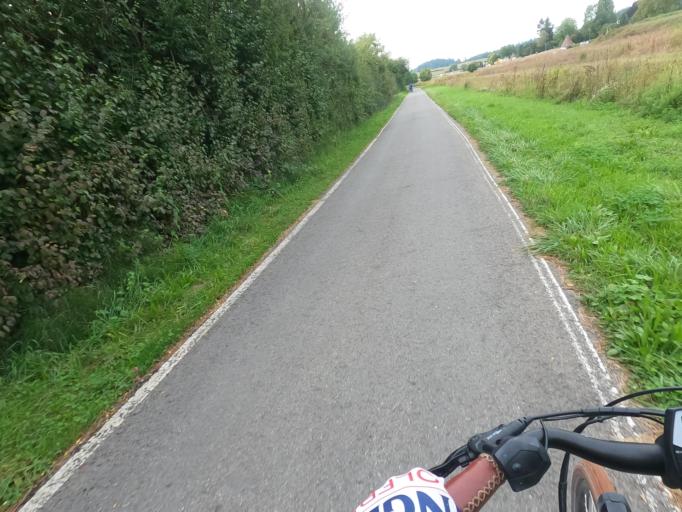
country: DE
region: Baden-Wuerttemberg
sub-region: Freiburg Region
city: Allensbach
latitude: 47.7044
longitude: 9.1039
